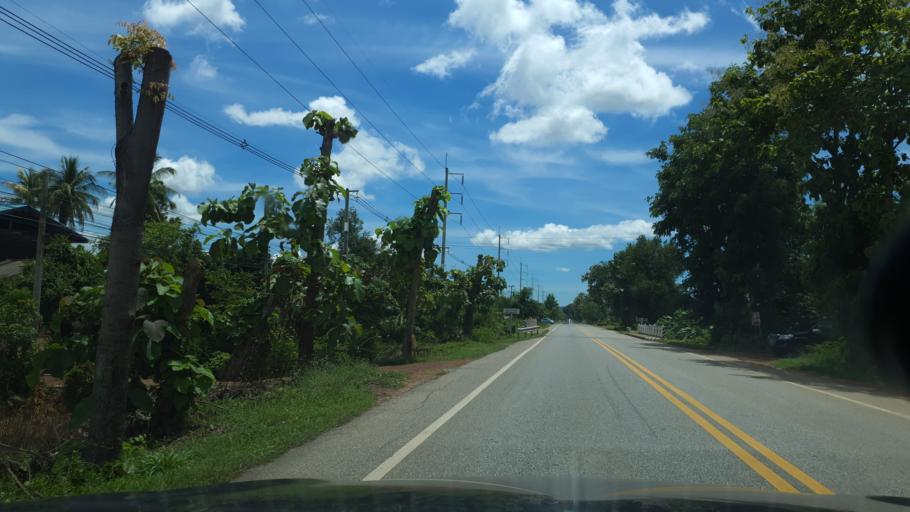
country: TH
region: Sukhothai
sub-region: Amphoe Si Satchanalai
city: Si Satchanalai
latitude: 17.4946
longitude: 99.7592
